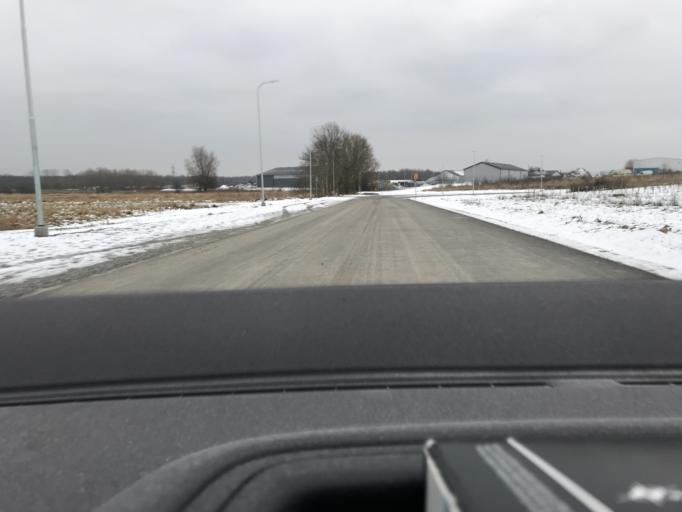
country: SE
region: Skane
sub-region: Ystads Kommun
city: Ystad
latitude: 55.4482
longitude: 13.8550
